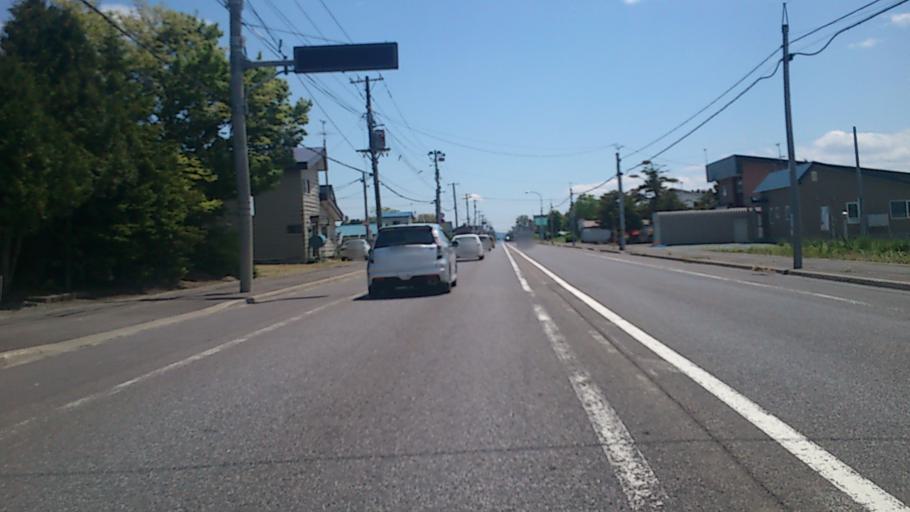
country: JP
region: Hokkaido
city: Nayoro
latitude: 44.2460
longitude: 142.3948
